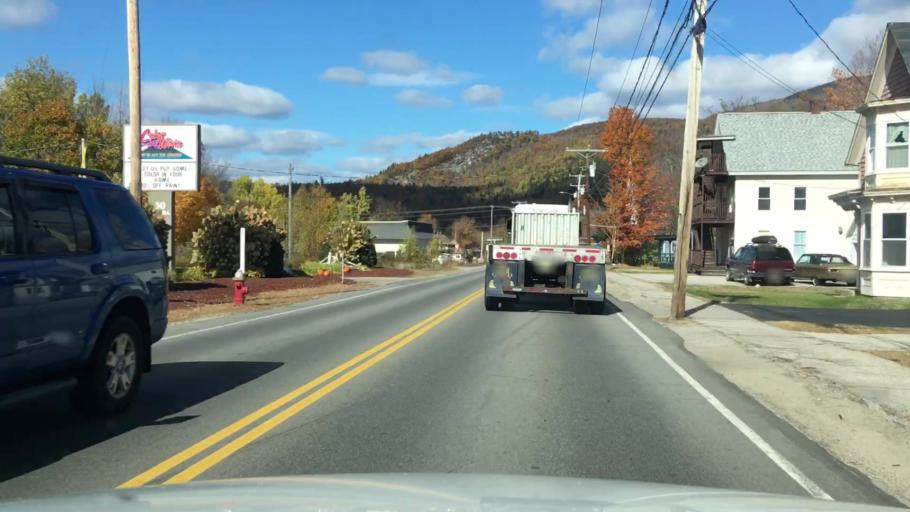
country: US
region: New Hampshire
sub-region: Coos County
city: Gorham
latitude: 44.3851
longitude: -71.1726
